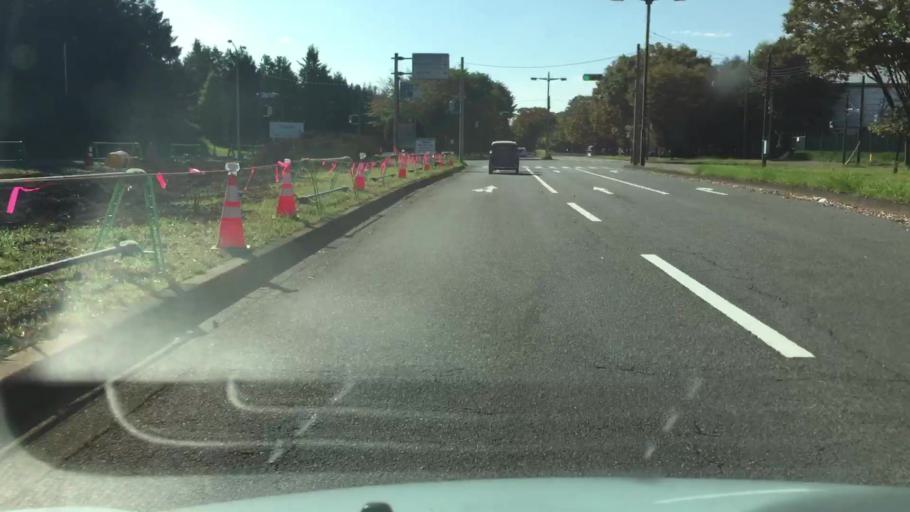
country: JP
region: Tochigi
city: Utsunomiya-shi
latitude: 36.5484
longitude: 139.9847
